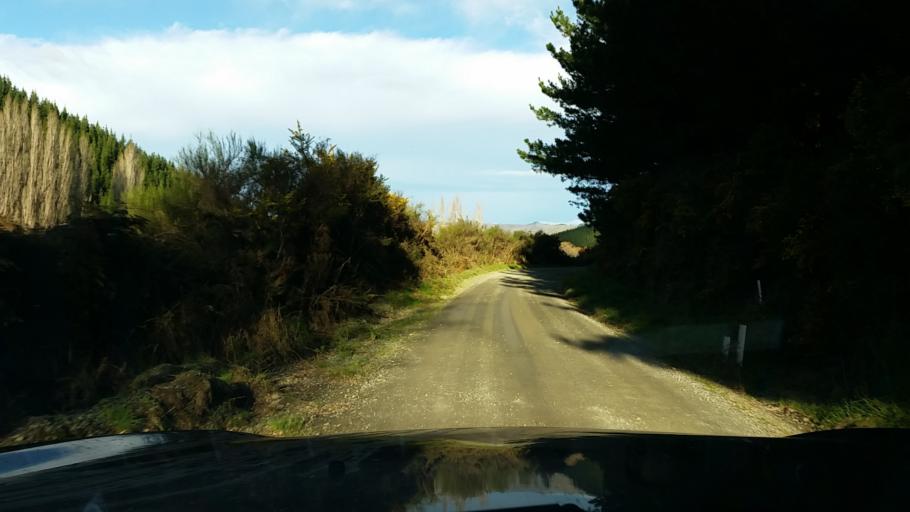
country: NZ
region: Nelson
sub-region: Nelson City
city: Nelson
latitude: -41.5557
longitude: 173.4288
